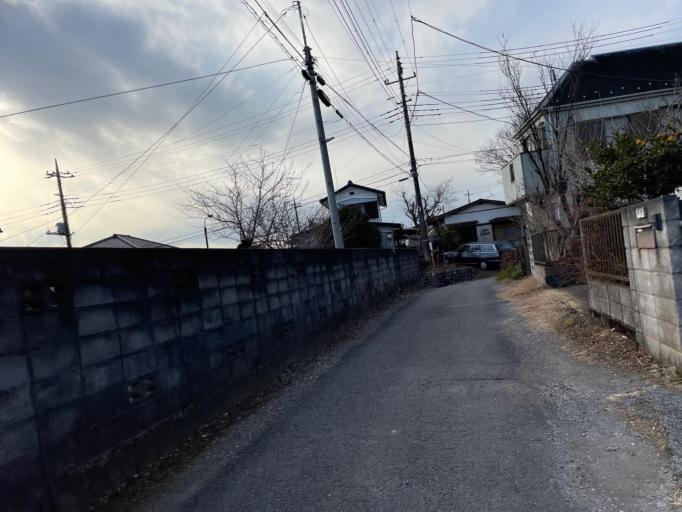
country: JP
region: Saitama
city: Hanno
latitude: 35.8414
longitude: 139.3394
